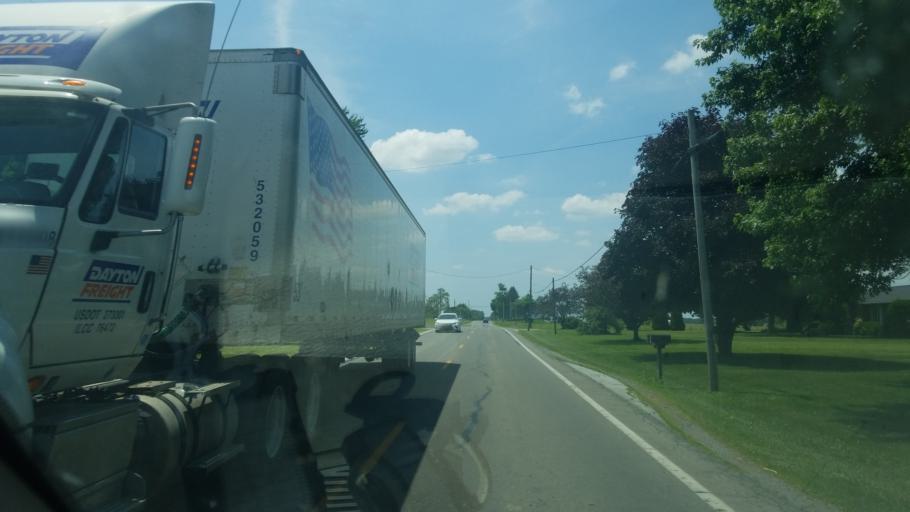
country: US
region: Ohio
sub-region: Hardin County
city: Ada
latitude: 40.7765
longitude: -83.8522
